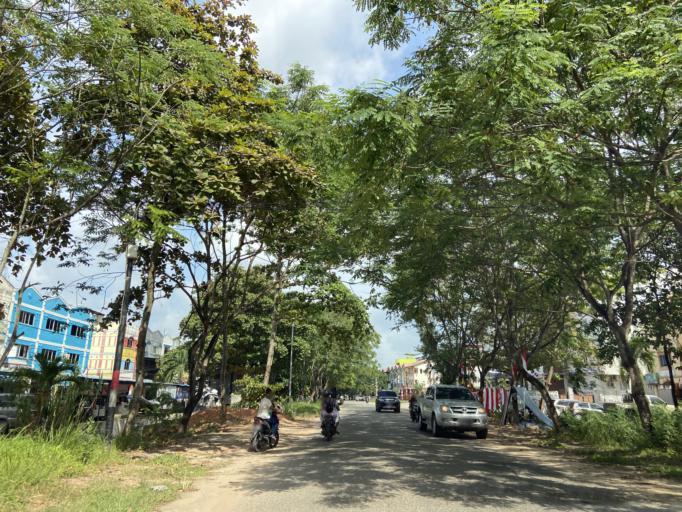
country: SG
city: Singapore
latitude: 1.1343
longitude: 104.0335
